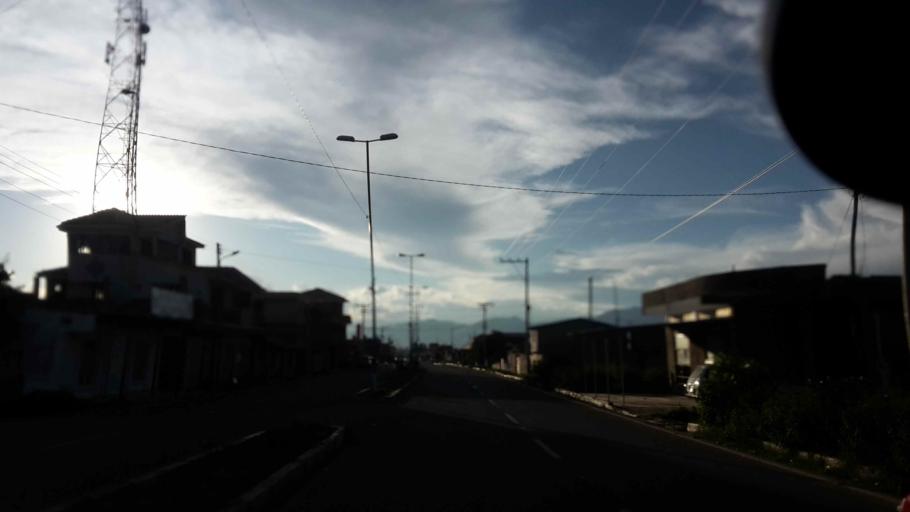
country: BO
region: Cochabamba
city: Arani
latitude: -17.5698
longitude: -65.7715
